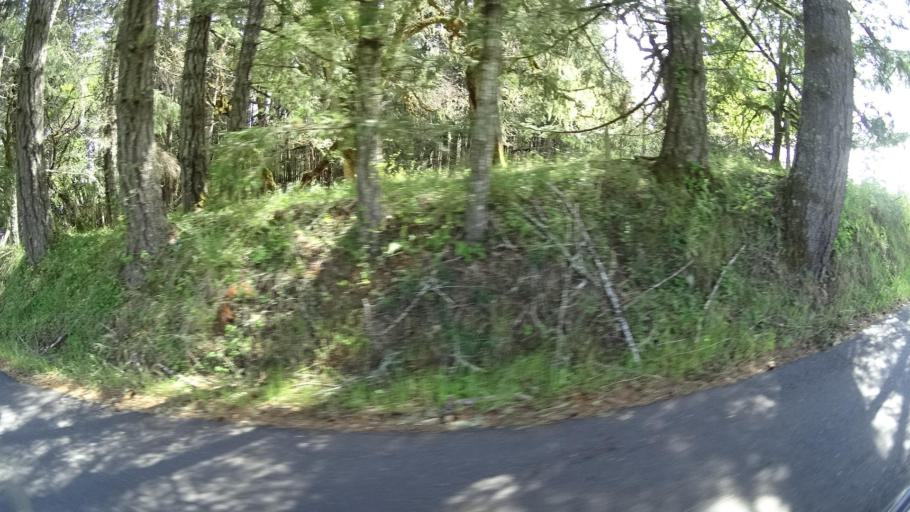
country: US
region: California
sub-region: Humboldt County
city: Redway
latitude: 40.4083
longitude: -123.7518
